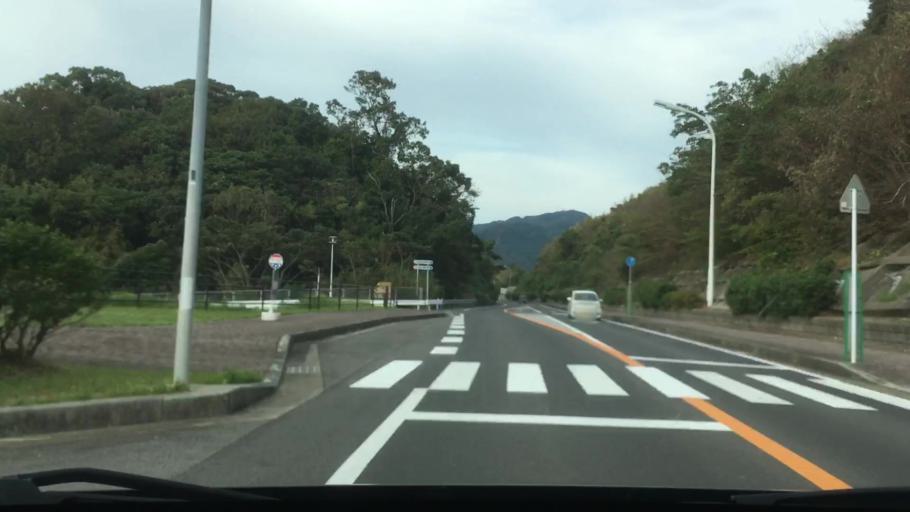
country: JP
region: Nagasaki
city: Sasebo
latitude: 33.0379
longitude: 129.6362
